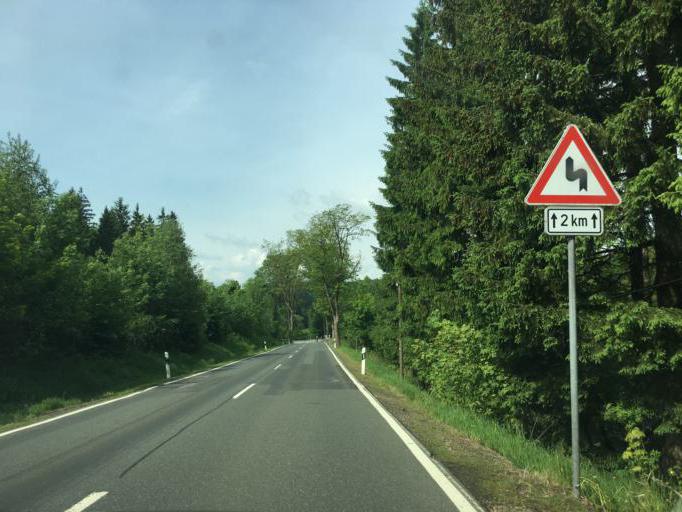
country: DE
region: Saxony
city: Frauenstein
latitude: 50.7872
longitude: 13.5458
